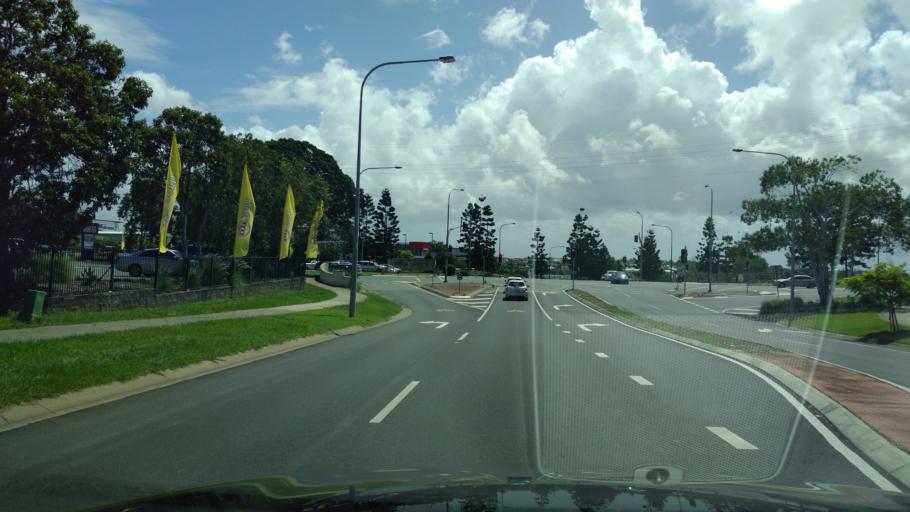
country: AU
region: Queensland
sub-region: Moreton Bay
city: Mango Hill
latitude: -27.2424
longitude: 153.0252
